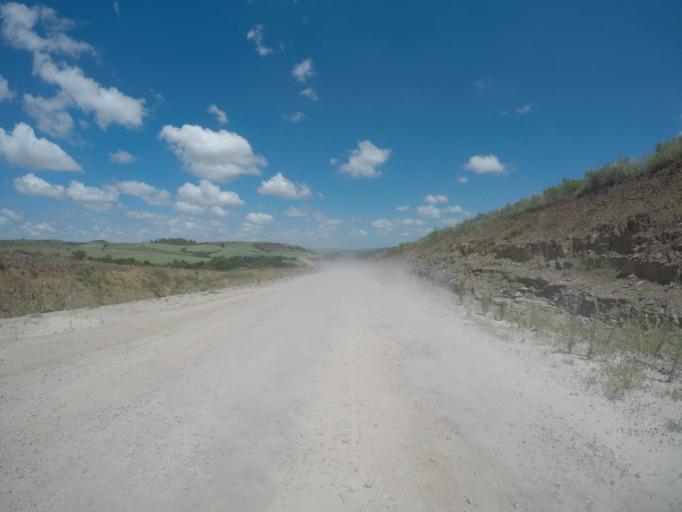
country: ZA
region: KwaZulu-Natal
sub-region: uThungulu District Municipality
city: Empangeni
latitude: -28.6378
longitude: 31.7637
